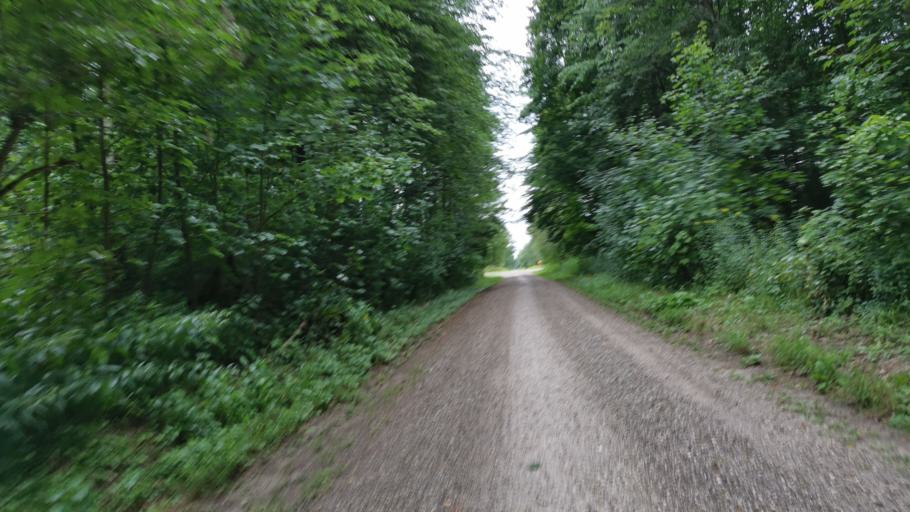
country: DE
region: Bavaria
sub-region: Upper Bavaria
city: Unterhaching
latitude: 48.0644
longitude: 11.5736
